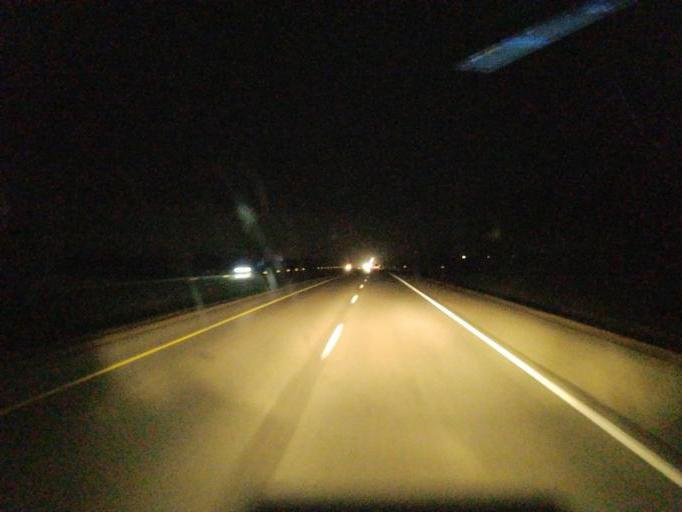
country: US
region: Iowa
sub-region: Madison County
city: Earlham
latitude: 41.5178
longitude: -94.1762
